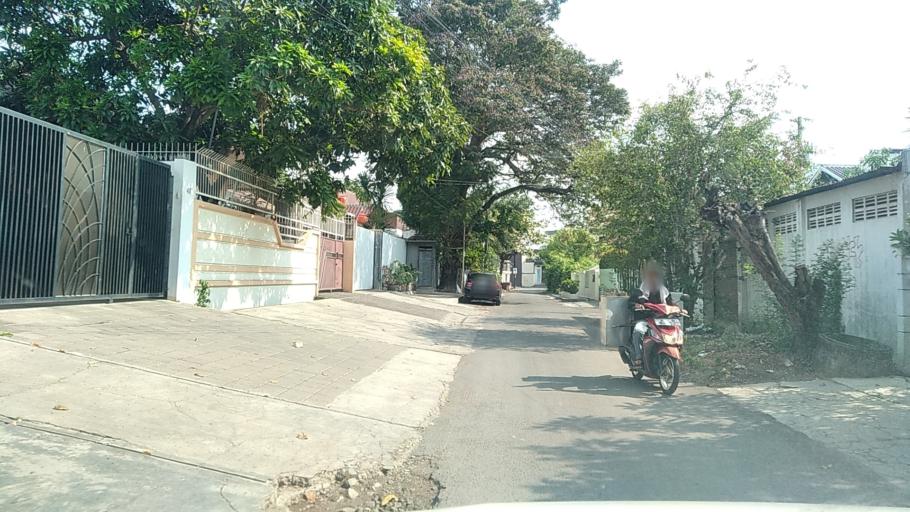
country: ID
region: Central Java
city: Semarang
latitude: -6.9885
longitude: 110.4390
